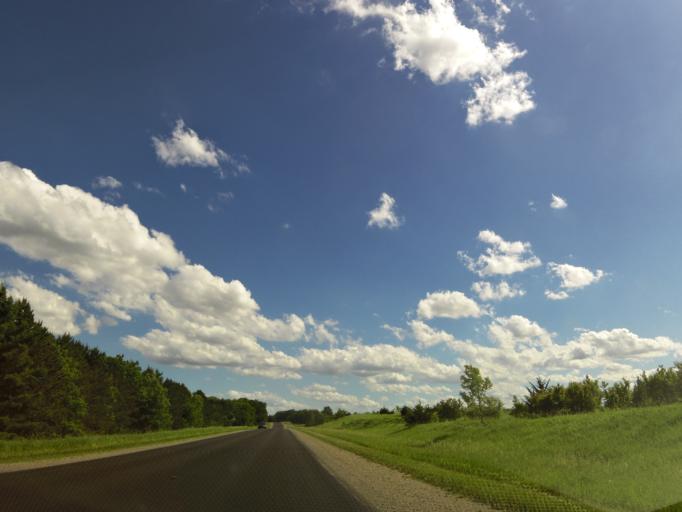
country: US
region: Minnesota
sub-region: Meeker County
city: Dassel
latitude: 45.1350
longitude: -94.2968
